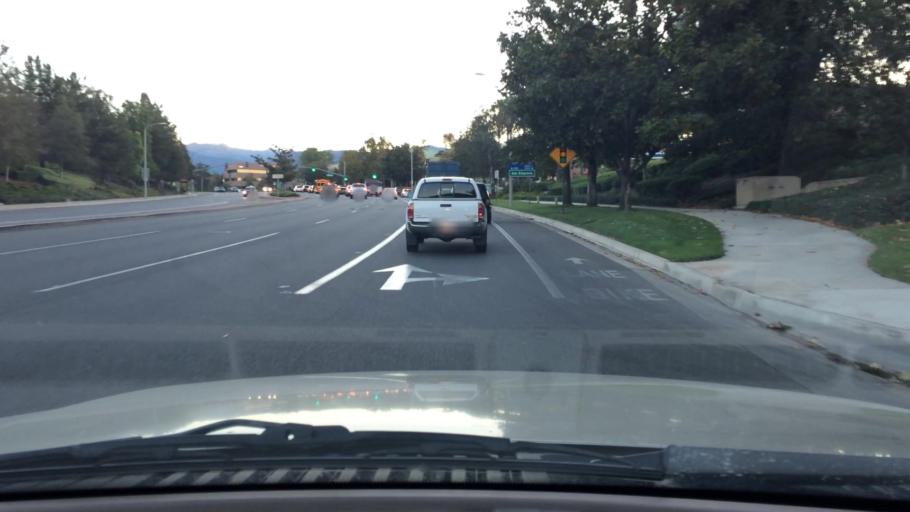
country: US
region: California
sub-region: Orange County
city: Rancho Santa Margarita
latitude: 33.6375
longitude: -117.6104
